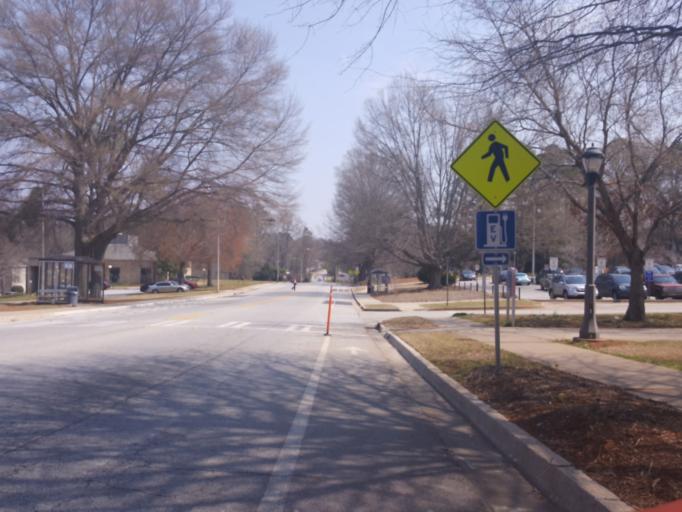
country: US
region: Georgia
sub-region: Carroll County
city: Carrollton
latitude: 33.5754
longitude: -85.0973
